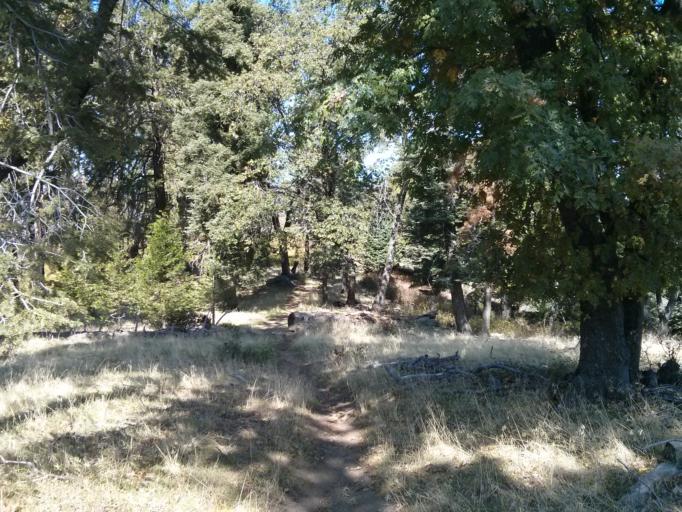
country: US
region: California
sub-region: Riverside County
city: Aguanga
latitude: 33.3376
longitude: -116.9070
